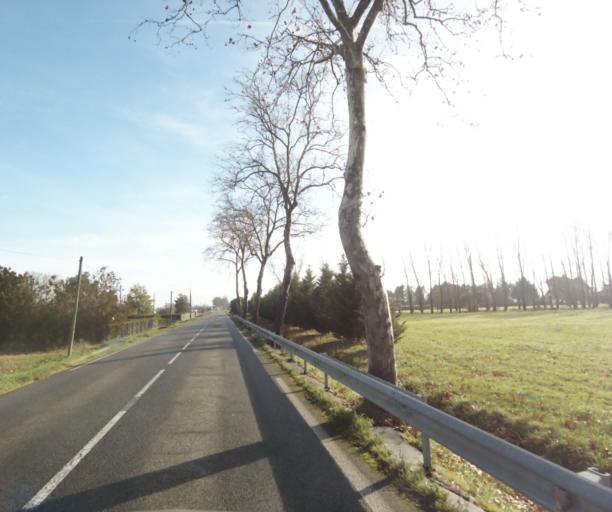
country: FR
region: Midi-Pyrenees
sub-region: Departement du Tarn-et-Garonne
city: Nohic
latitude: 43.8759
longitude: 1.4574
